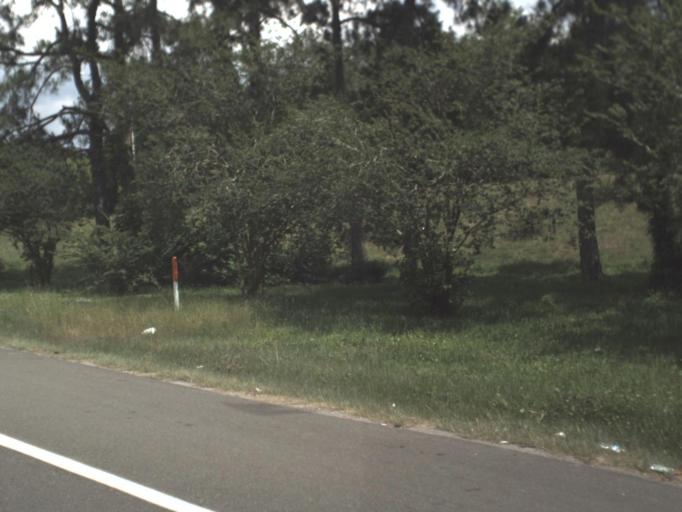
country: US
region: Florida
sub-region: Duval County
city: Jacksonville
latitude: 30.3560
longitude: -81.6681
